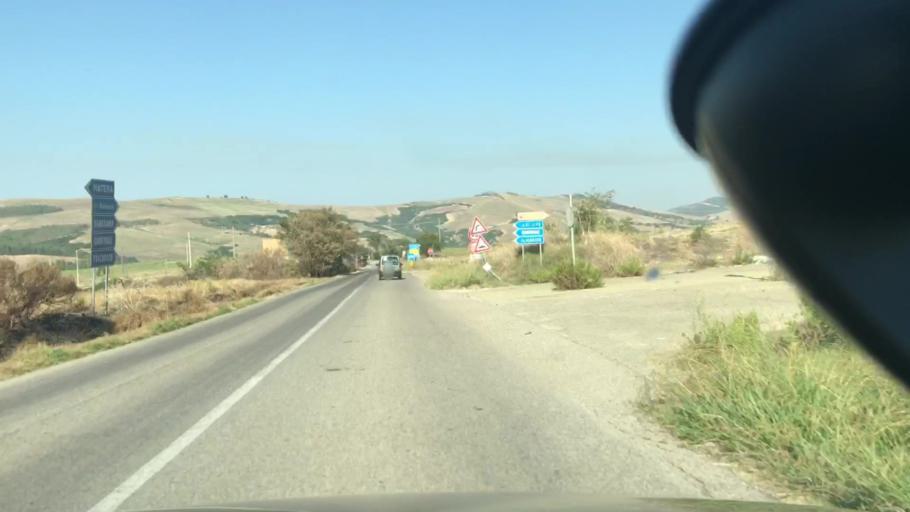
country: IT
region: Basilicate
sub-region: Provincia di Matera
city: La Martella
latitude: 40.6744
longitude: 16.4594
